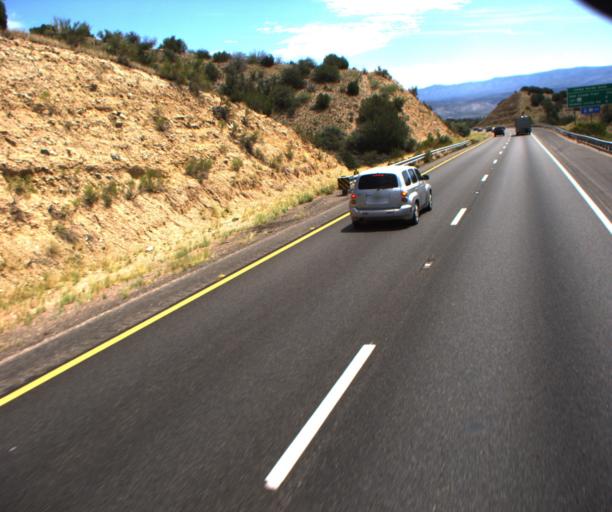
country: US
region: Arizona
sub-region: Yavapai County
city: Camp Verde
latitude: 34.5375
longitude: -111.9141
